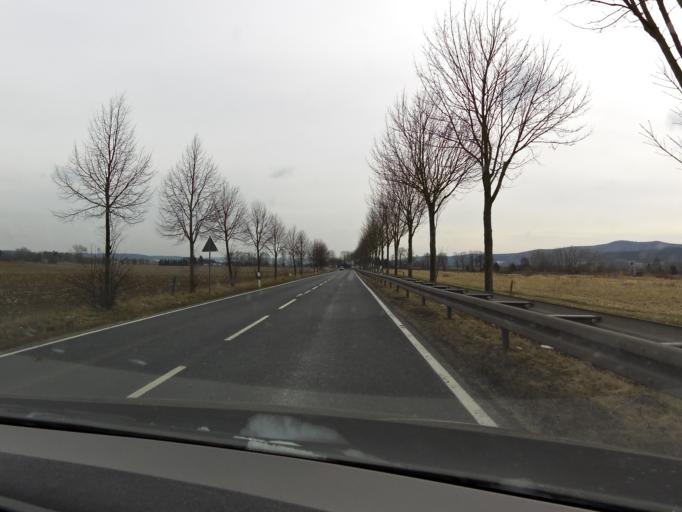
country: DE
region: Thuringia
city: Breitungen
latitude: 50.7791
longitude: 10.3113
